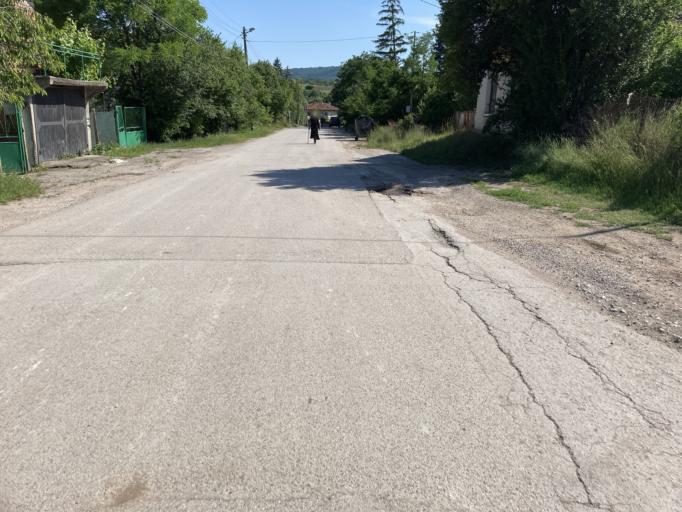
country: BG
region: Sofiya
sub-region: Obshtina Slivnitsa
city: Slivnitsa
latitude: 42.8518
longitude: 22.9815
